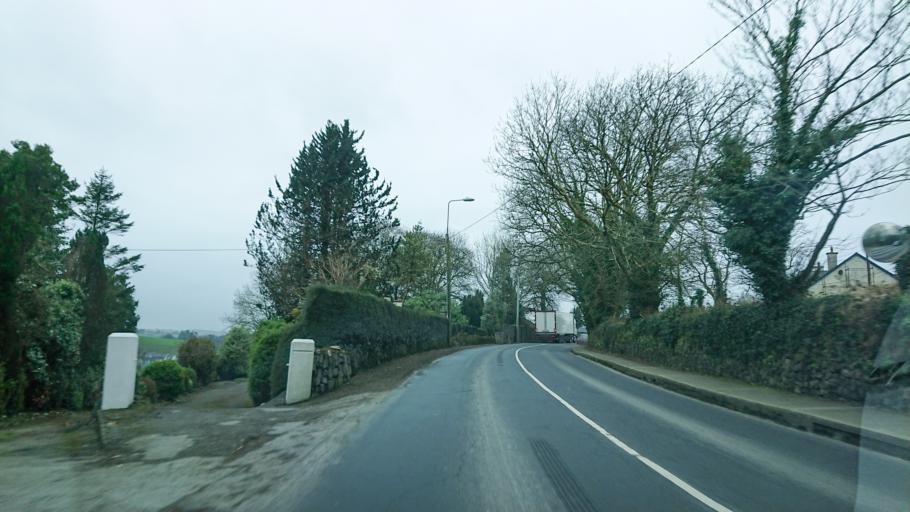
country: IE
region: Munster
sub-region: County Cork
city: Bandon
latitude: 51.7474
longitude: -8.7505
